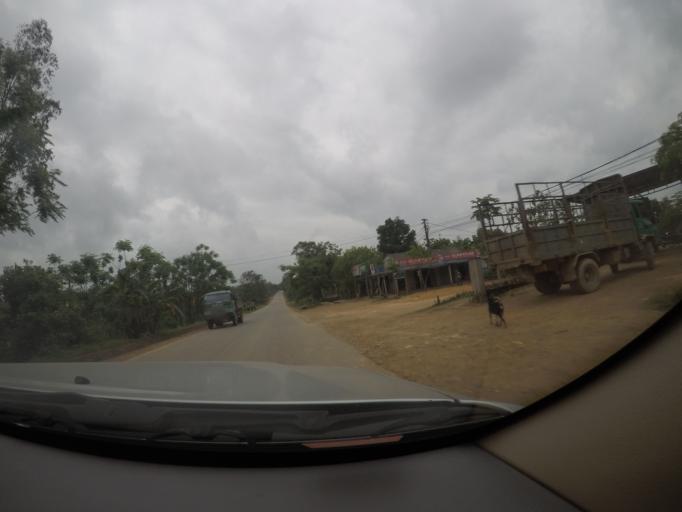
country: VN
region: Quang Tri
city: Cam Lo
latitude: 16.8829
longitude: 106.9928
